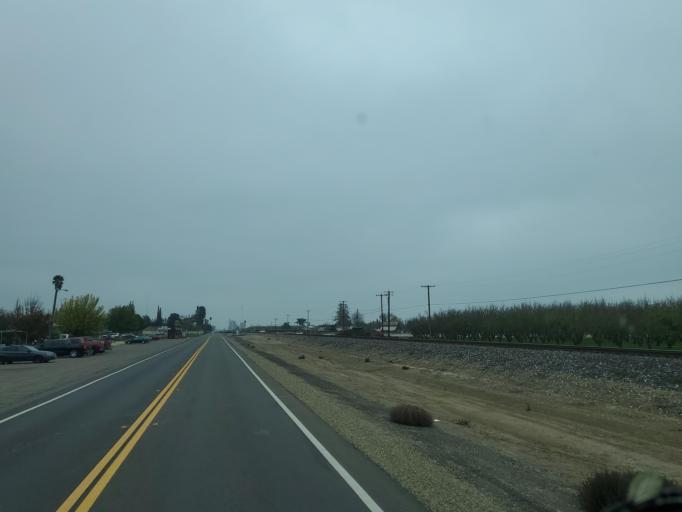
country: US
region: California
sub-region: Stanislaus County
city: Hughson
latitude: 37.5909
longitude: -120.8630
